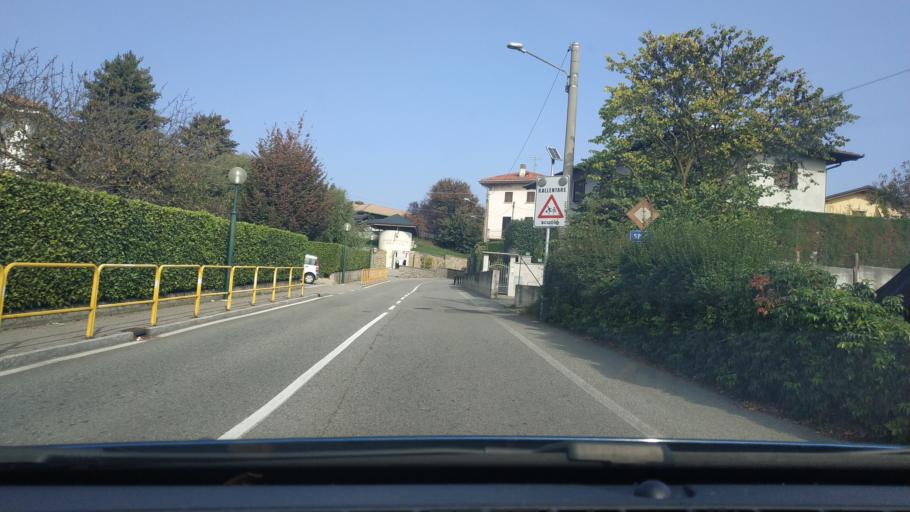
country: IT
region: Piedmont
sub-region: Provincia di Torino
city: Romano Canavese
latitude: 45.3887
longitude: 7.8651
